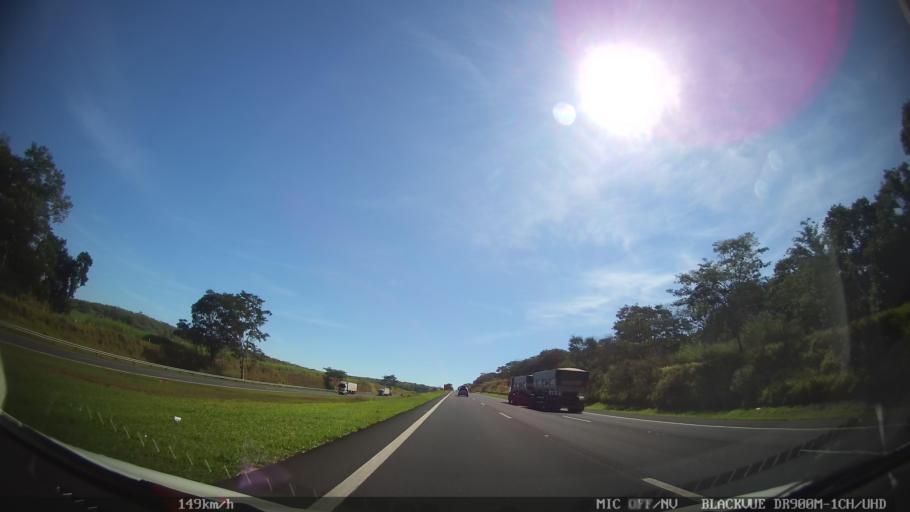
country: BR
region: Sao Paulo
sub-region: Santa Rita Do Passa Quatro
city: Santa Rita do Passa Quatro
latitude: -21.7166
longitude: -47.5900
